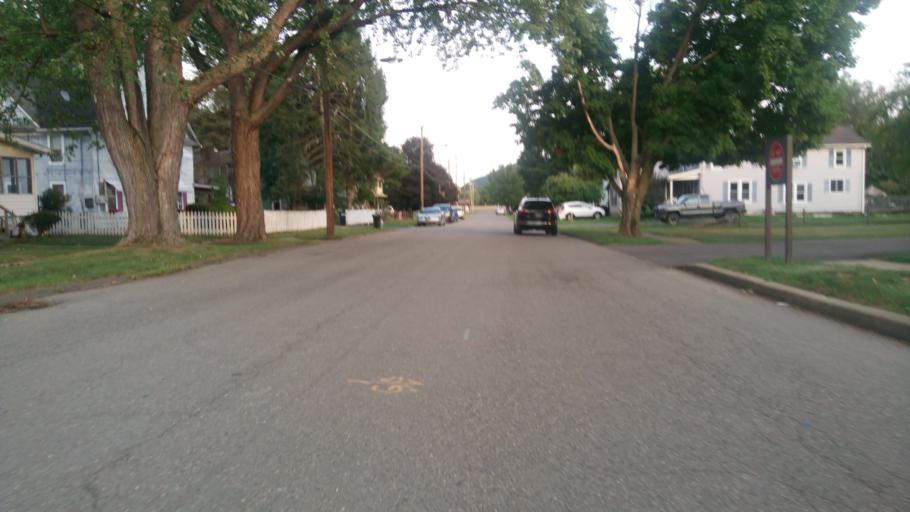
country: US
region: New York
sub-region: Chemung County
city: Southport
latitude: 42.0614
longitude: -76.8085
